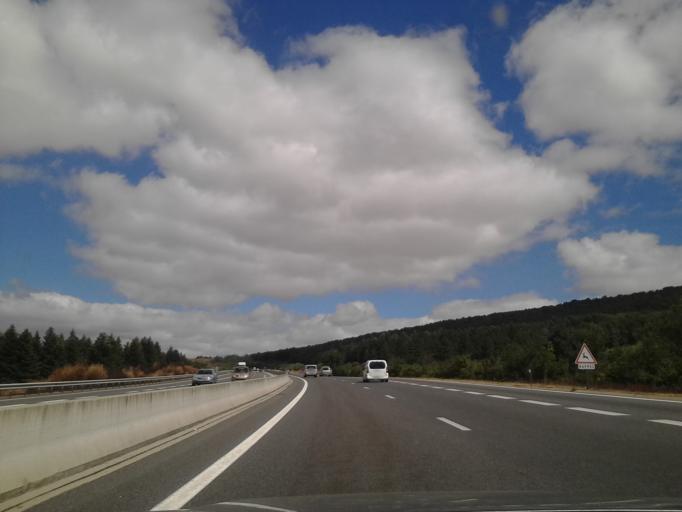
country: FR
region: Midi-Pyrenees
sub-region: Departement de l'Aveyron
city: Severac-le-Chateau
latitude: 44.2207
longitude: 3.0722
